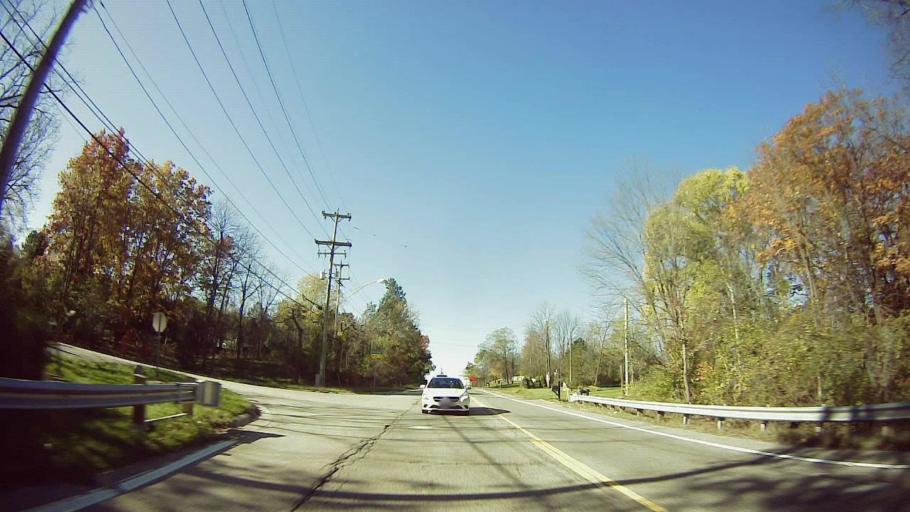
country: US
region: Michigan
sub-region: Oakland County
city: Franklin
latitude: 42.5436
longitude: -83.3374
